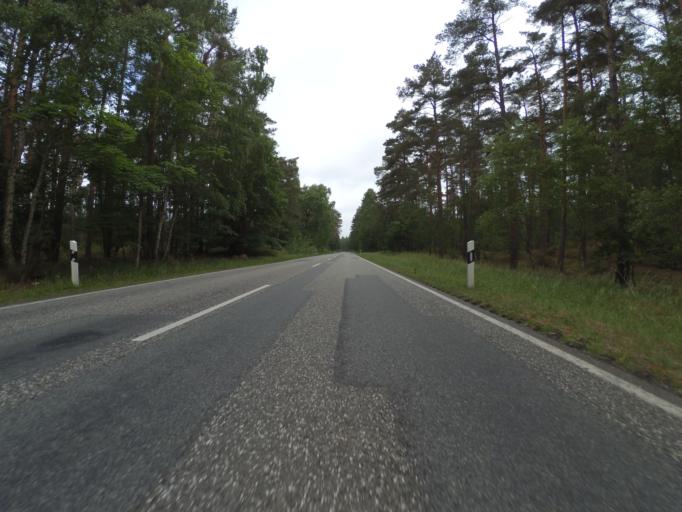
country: DE
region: Mecklenburg-Vorpommern
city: Krakow am See
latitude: 53.5748
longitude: 12.2709
